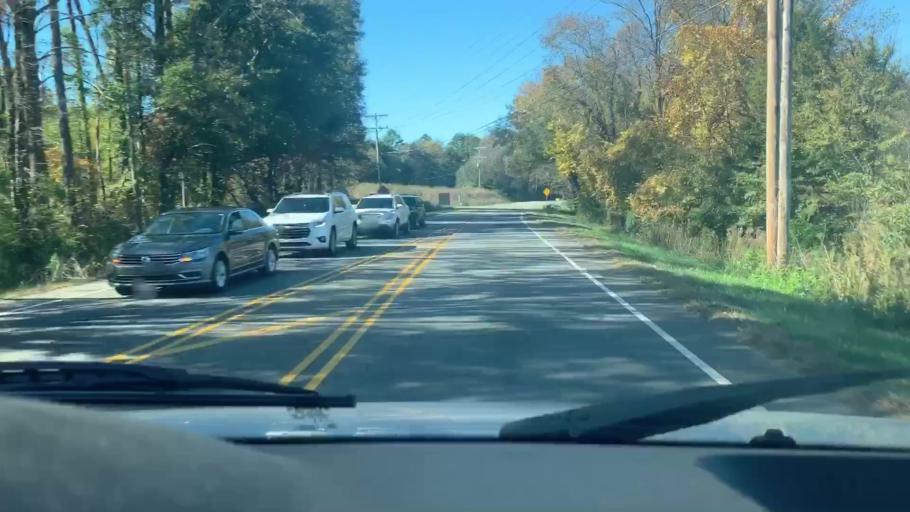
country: US
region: North Carolina
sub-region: Mecklenburg County
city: Huntersville
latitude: 35.4266
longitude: -80.9188
